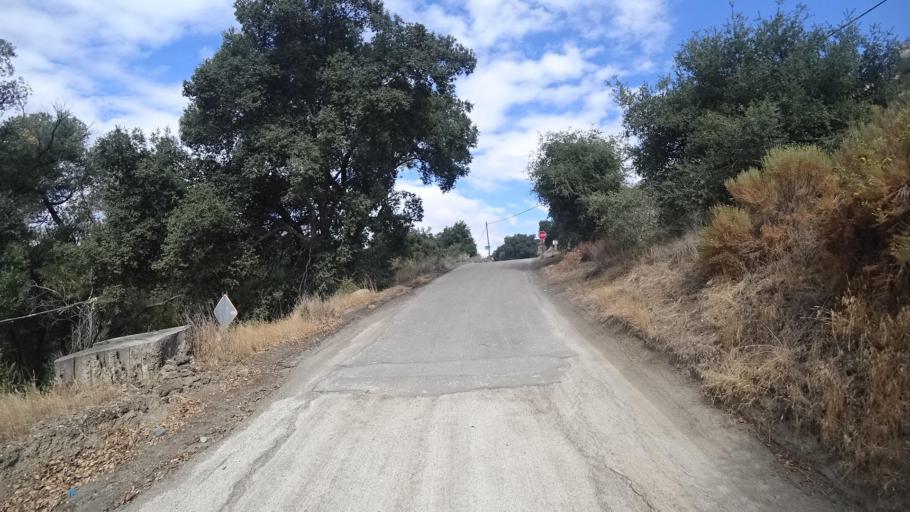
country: US
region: California
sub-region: San Diego County
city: Campo
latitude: 32.6800
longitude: -116.3336
